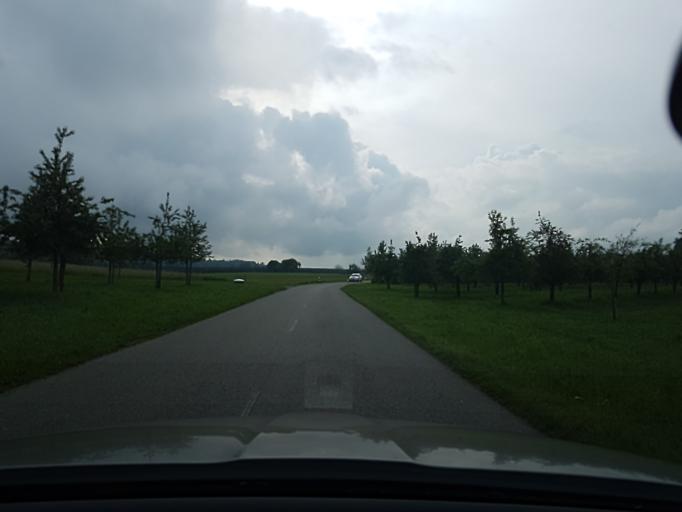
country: CH
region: Thurgau
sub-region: Arbon District
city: Roggwil
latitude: 47.5061
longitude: 9.3893
